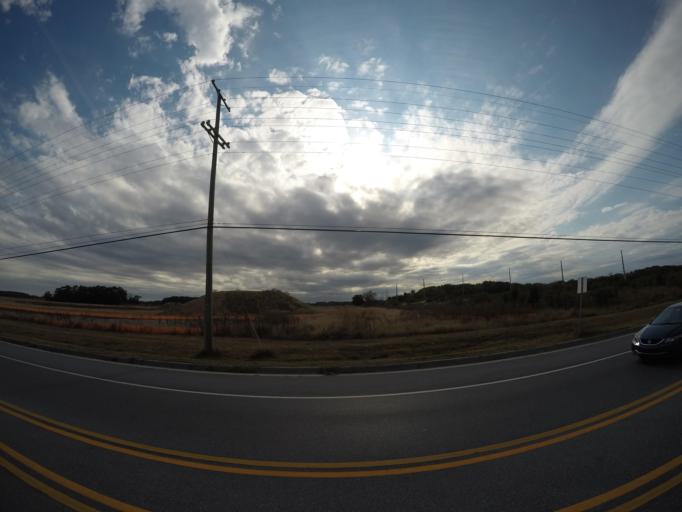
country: US
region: Delaware
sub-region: Sussex County
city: Lewes
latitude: 38.7317
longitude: -75.1522
